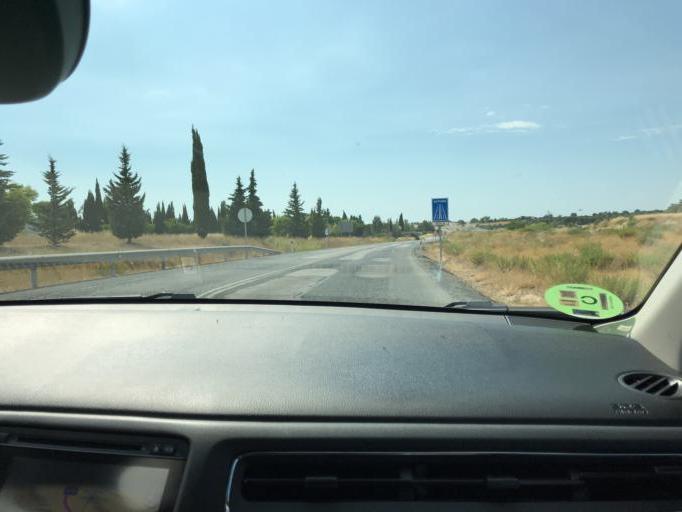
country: ES
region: Andalusia
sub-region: Provincia de Jaen
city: Ubeda
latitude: 38.0188
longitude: -3.4058
